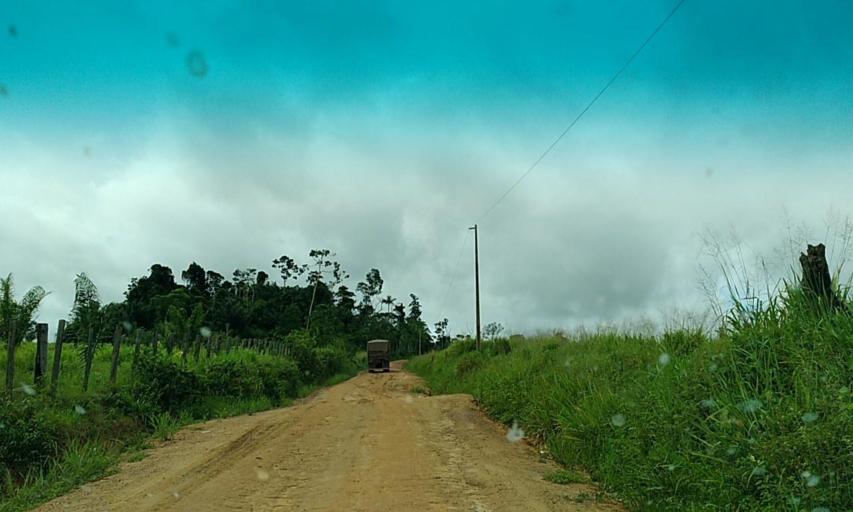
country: BR
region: Para
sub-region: Altamira
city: Altamira
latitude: -3.0726
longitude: -51.7086
